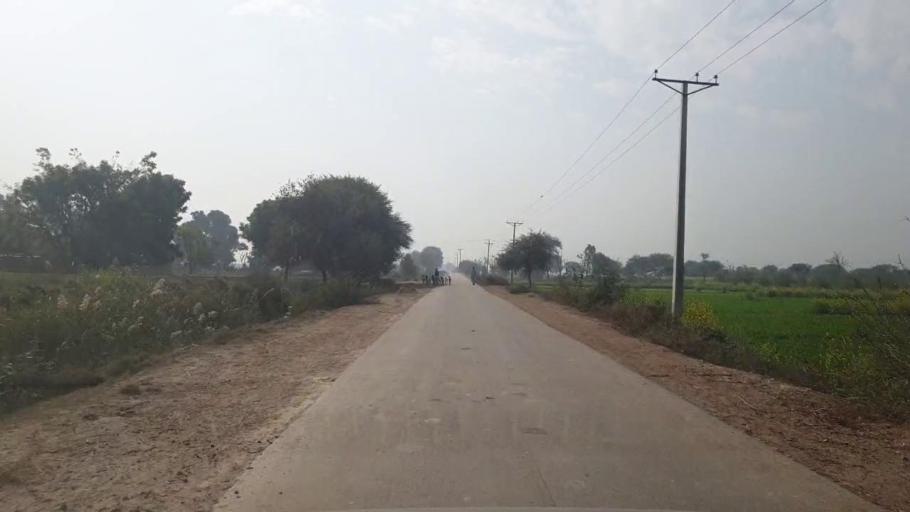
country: PK
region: Sindh
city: Hala
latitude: 25.7604
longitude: 68.4474
